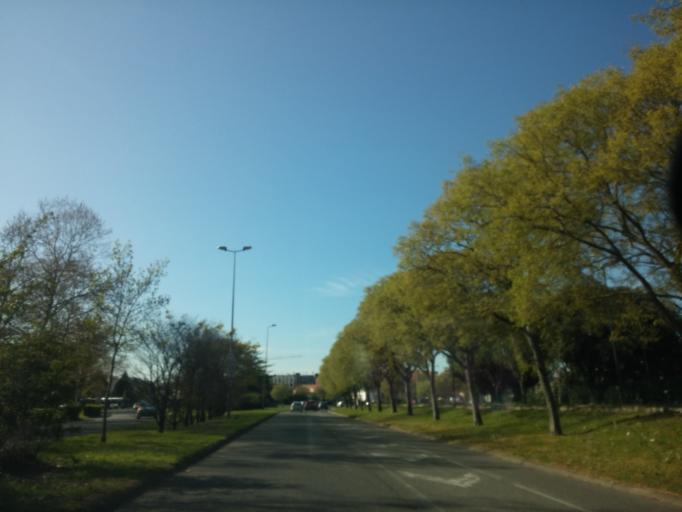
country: FR
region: Midi-Pyrenees
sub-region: Departement de la Haute-Garonne
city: Toulouse
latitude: 43.5733
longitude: 1.4064
